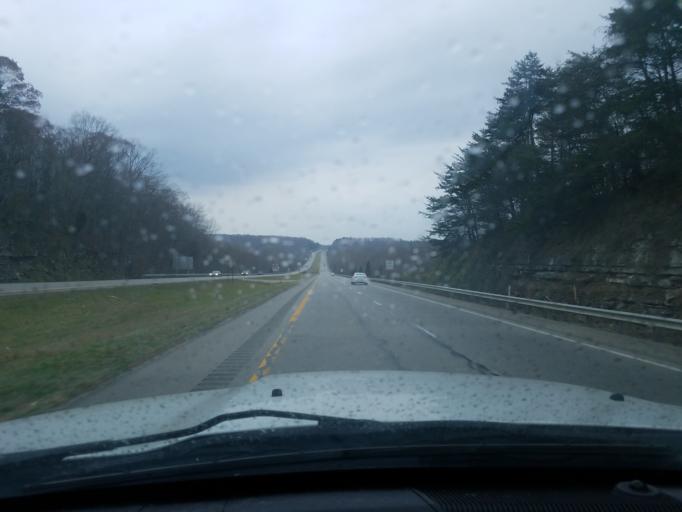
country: US
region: Kentucky
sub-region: Rowan County
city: Morehead
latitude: 38.1886
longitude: -83.4894
